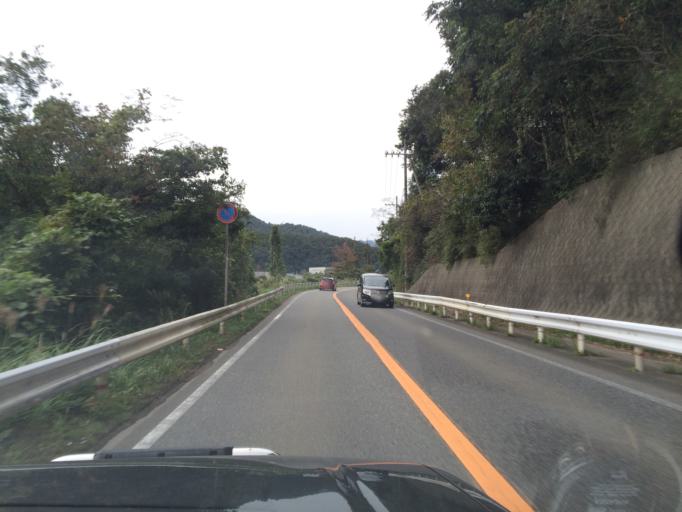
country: JP
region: Hyogo
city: Toyooka
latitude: 35.3964
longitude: 134.7907
